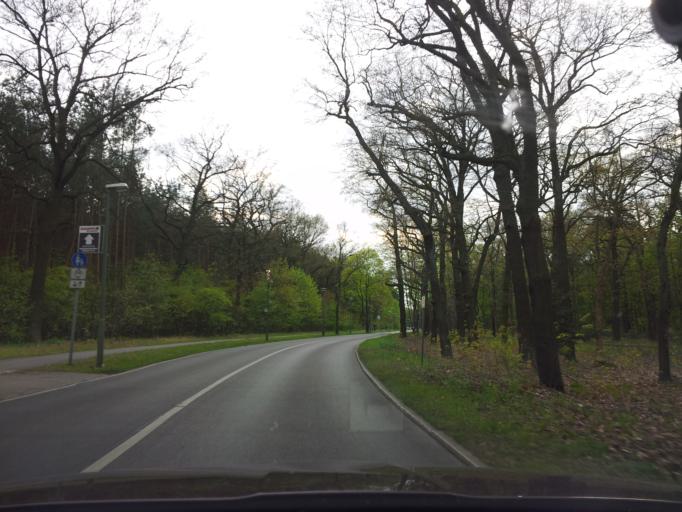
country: DE
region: Berlin
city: Friedrichshagen
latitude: 52.4739
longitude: 13.5993
